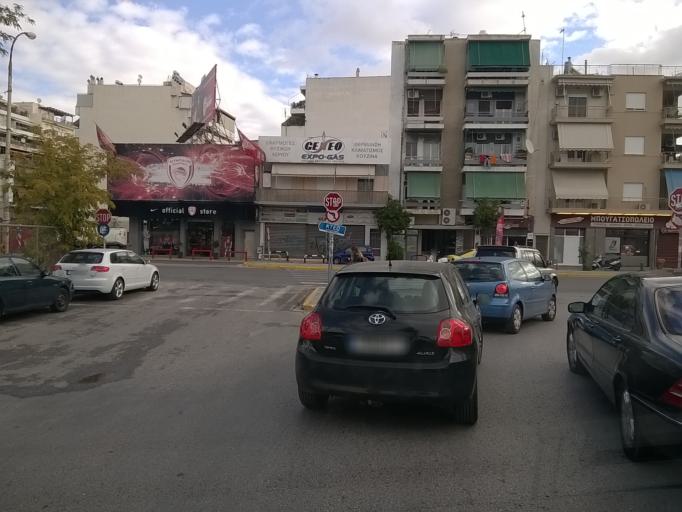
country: GR
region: Attica
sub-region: Nomarchia Athinas
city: Moskhaton
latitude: 37.9482
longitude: 23.6640
